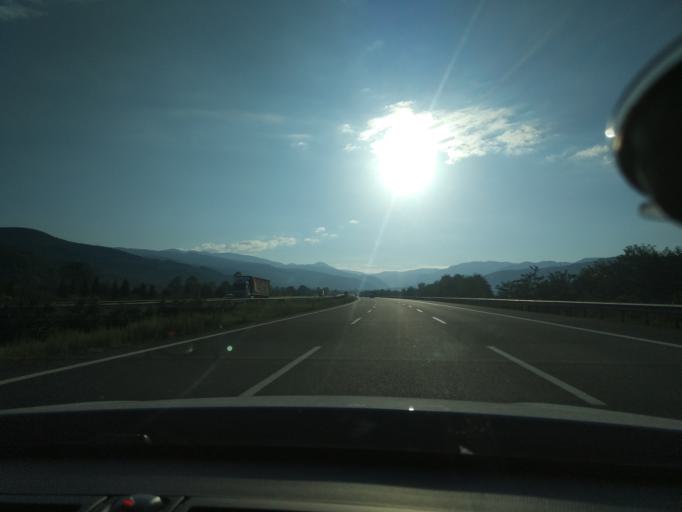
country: TR
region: Duzce
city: Kaynasli
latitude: 40.7845
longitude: 31.3016
